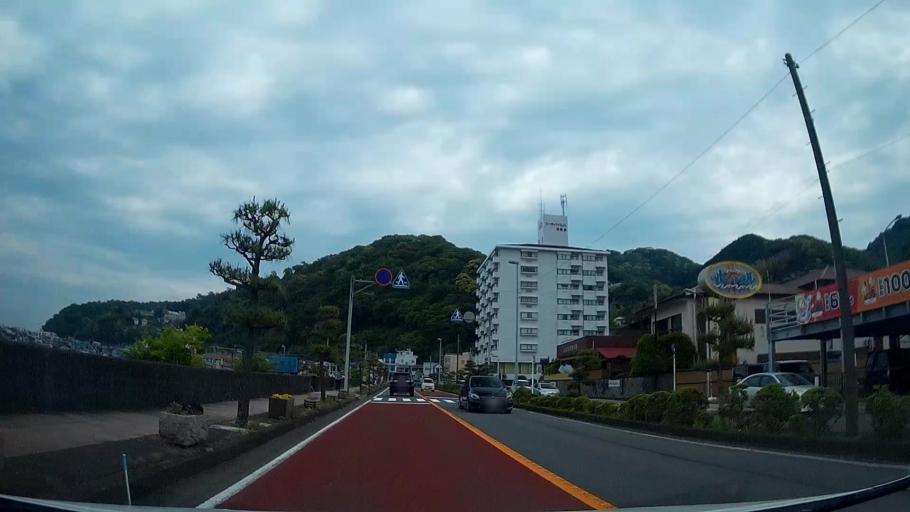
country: JP
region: Shizuoka
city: Atami
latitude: 35.0451
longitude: 139.0839
